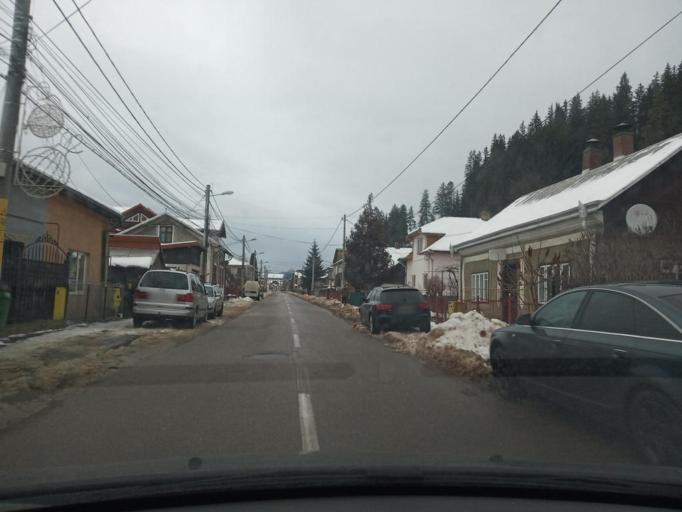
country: RO
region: Suceava
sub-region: Oras Gura Humorului
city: Gura Humorului
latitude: 47.5591
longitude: 25.8887
